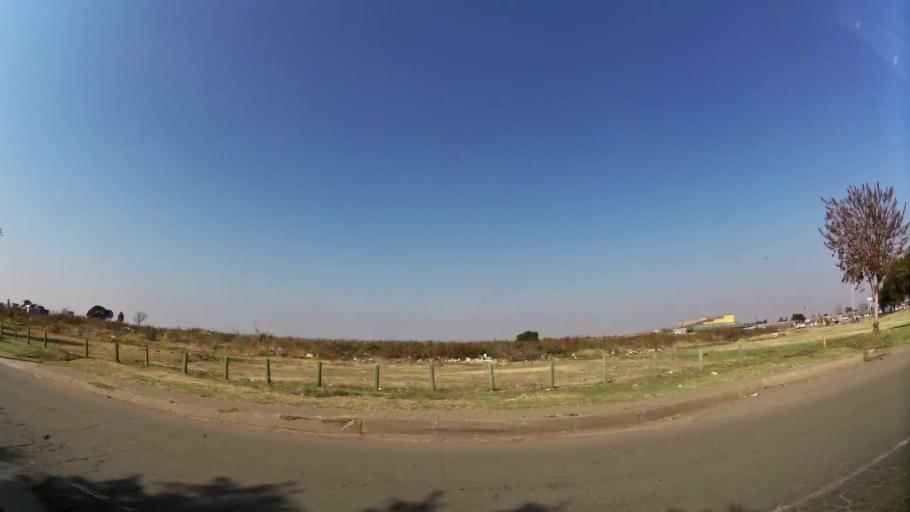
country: ZA
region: Gauteng
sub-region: Ekurhuleni Metropolitan Municipality
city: Boksburg
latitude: -26.2310
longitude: 28.2953
